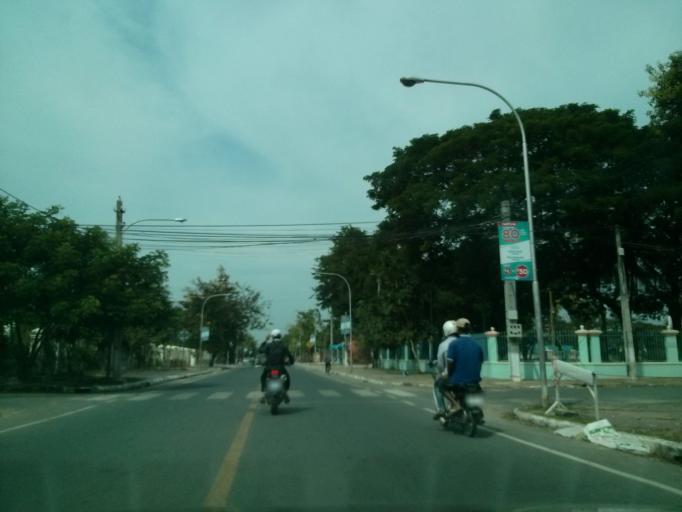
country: KH
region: Takeo
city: Takeo
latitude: 10.9900
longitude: 104.7834
